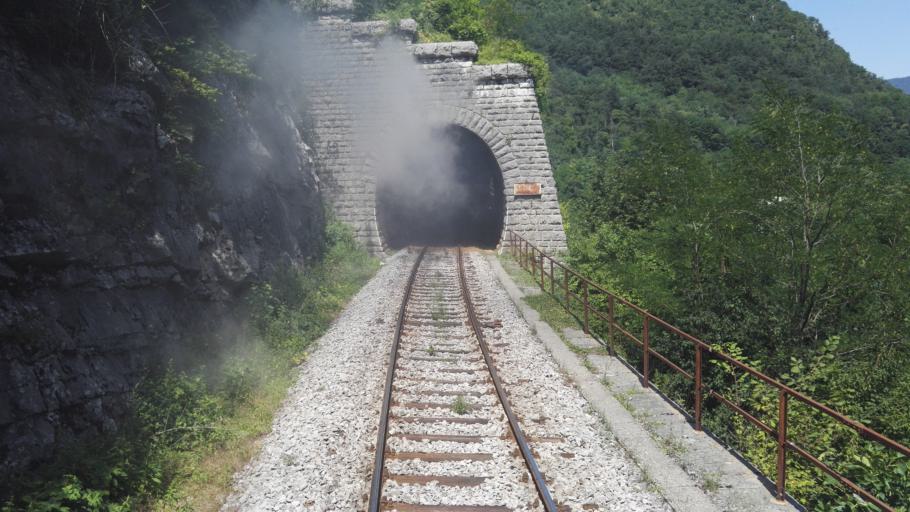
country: SI
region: Kanal
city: Deskle
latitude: 46.0170
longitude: 13.6060
